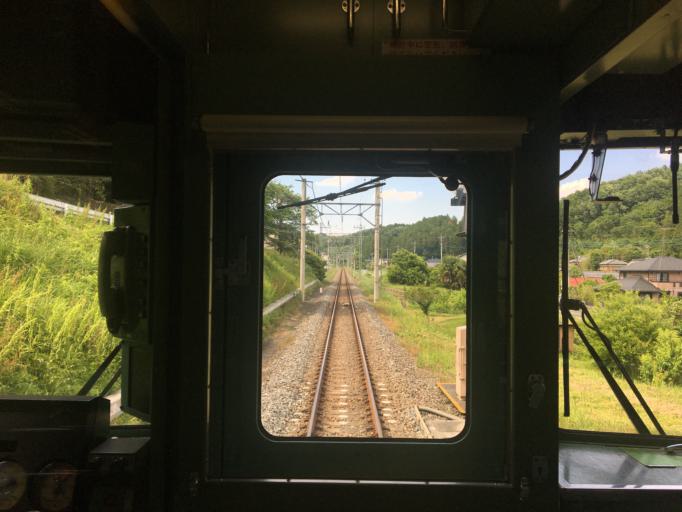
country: JP
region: Saitama
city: Ogawa
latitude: 36.0775
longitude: 139.2376
